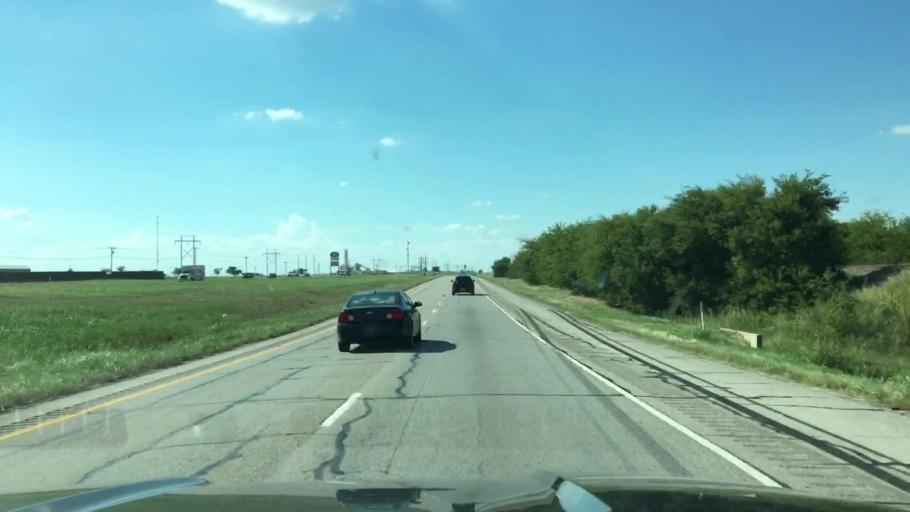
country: US
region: Texas
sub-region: Wise County
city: Decatur
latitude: 33.1728
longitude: -97.5390
